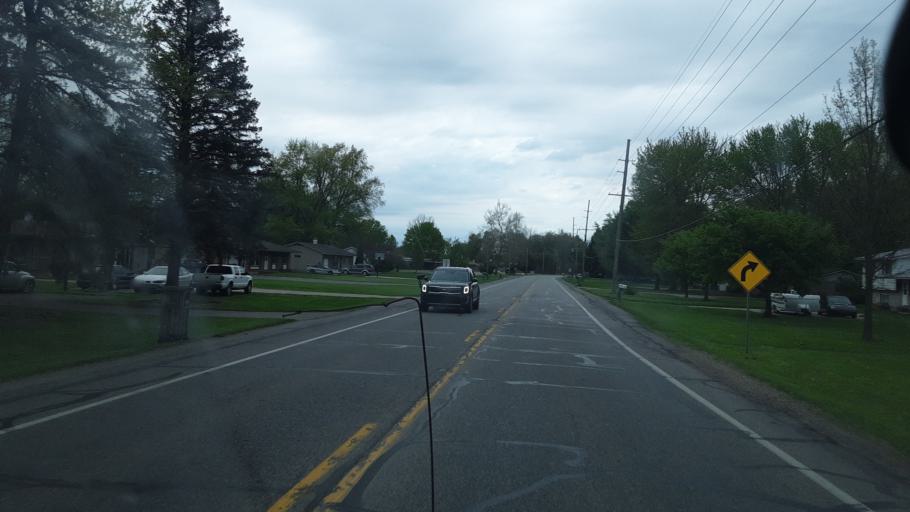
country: US
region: Indiana
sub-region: Elkhart County
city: Goshen
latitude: 41.6362
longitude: -85.8269
